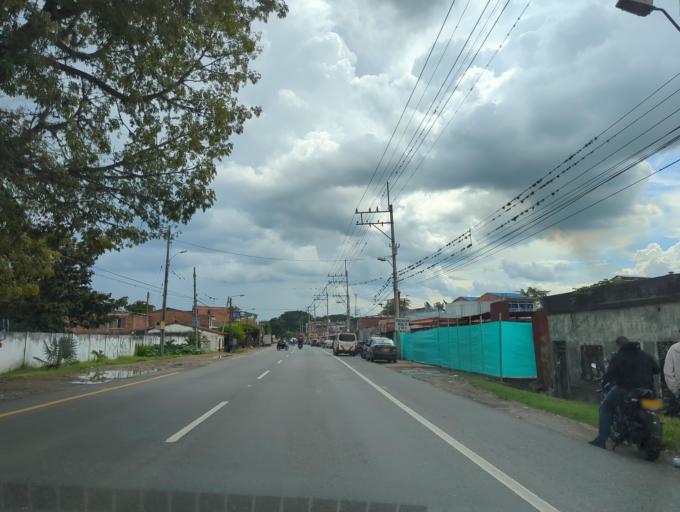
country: CO
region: Valle del Cauca
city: Zarzal
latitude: 4.3211
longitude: -76.0697
